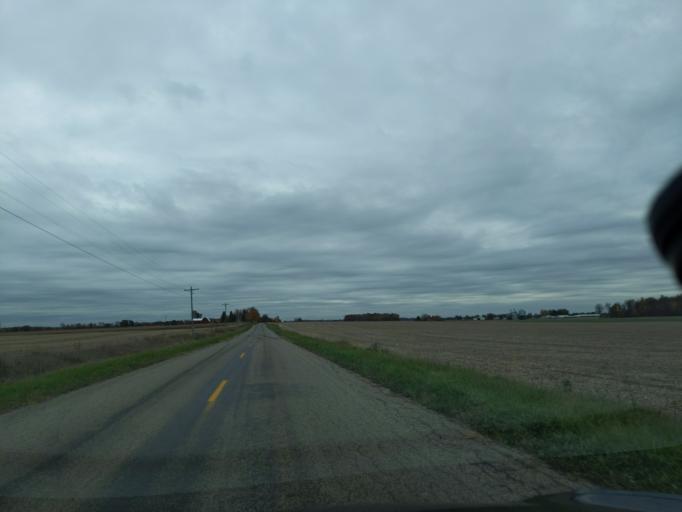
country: US
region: Michigan
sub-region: Eaton County
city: Eaton Rapids
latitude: 42.4470
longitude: -84.6006
